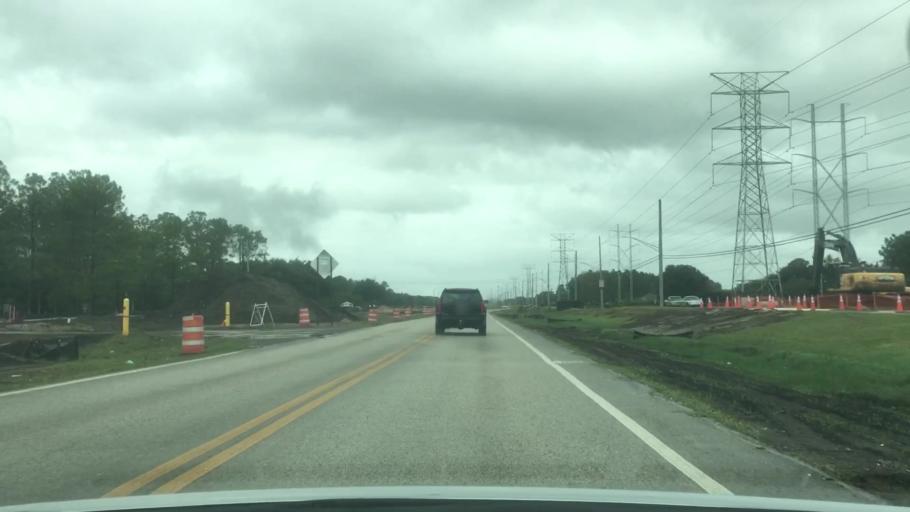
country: US
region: Florida
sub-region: Duval County
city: Atlantic Beach
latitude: 30.3256
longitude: -81.4894
